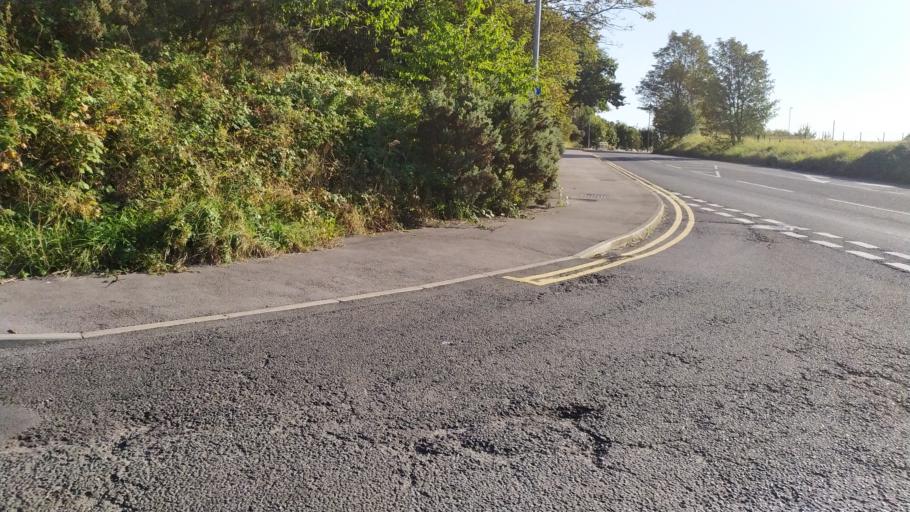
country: GB
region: England
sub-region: City and Borough of Leeds
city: Chapel Allerton
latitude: 53.8417
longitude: -1.5576
